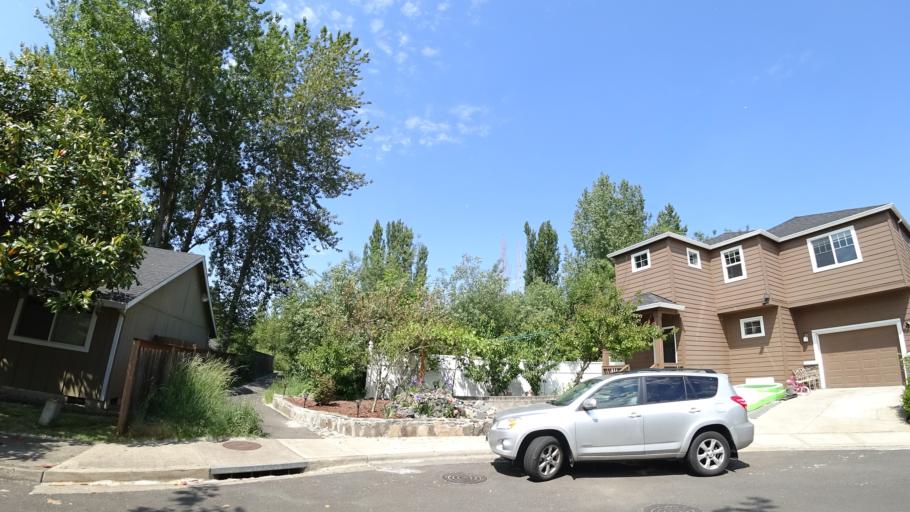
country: US
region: Oregon
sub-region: Washington County
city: Garden Home-Whitford
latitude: 45.4554
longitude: -122.7537
